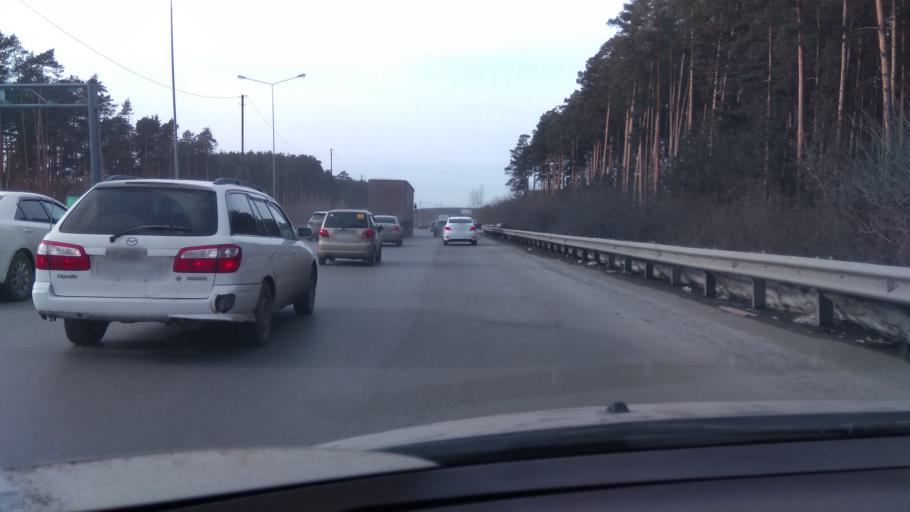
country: RU
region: Sverdlovsk
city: Shirokaya Rechka
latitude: 56.8138
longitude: 60.5162
